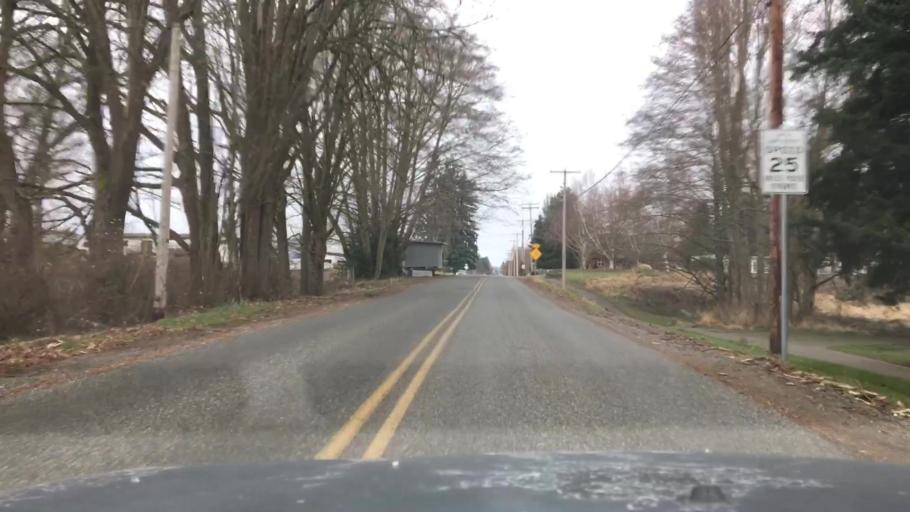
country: US
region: Washington
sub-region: Skagit County
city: Sedro-Woolley
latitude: 48.4921
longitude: -122.2260
